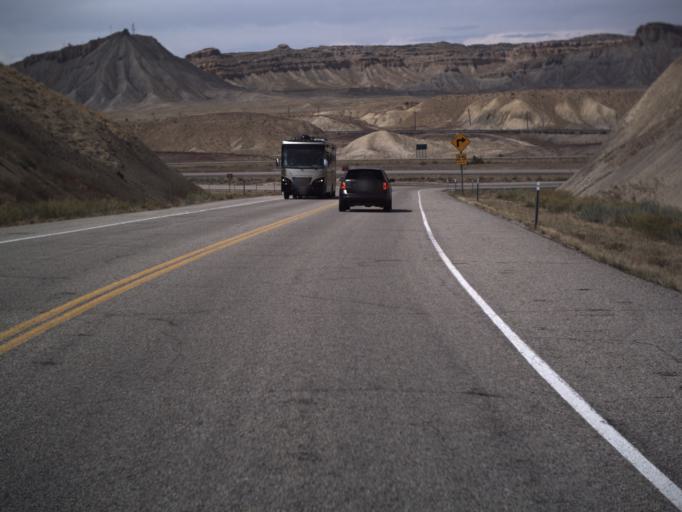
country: US
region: Utah
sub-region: Grand County
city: Moab
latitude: 38.9365
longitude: -109.8313
